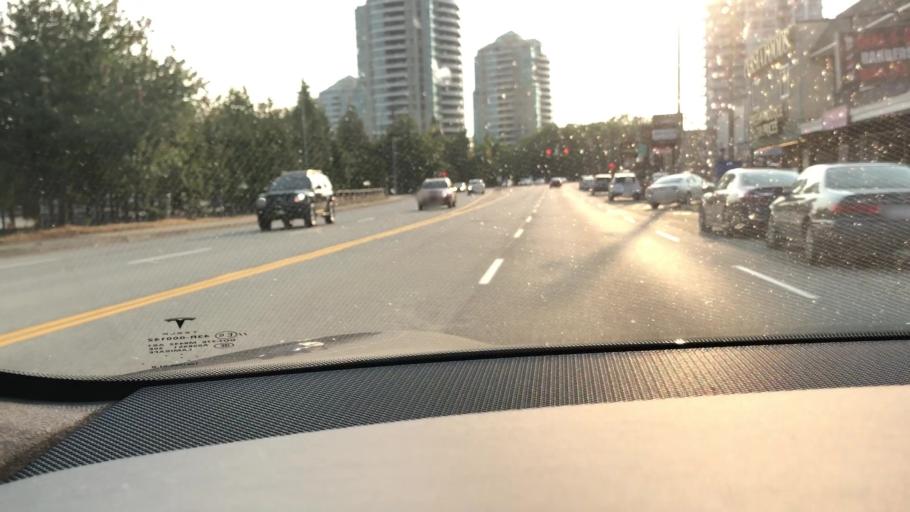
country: CA
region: British Columbia
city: Burnaby
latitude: 49.2182
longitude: -122.9622
